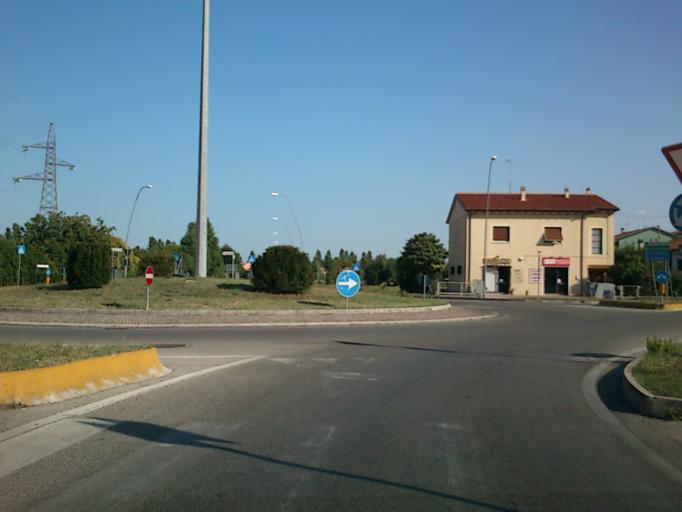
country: IT
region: The Marches
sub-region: Provincia di Pesaro e Urbino
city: Fano
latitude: 43.8353
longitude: 13.0094
